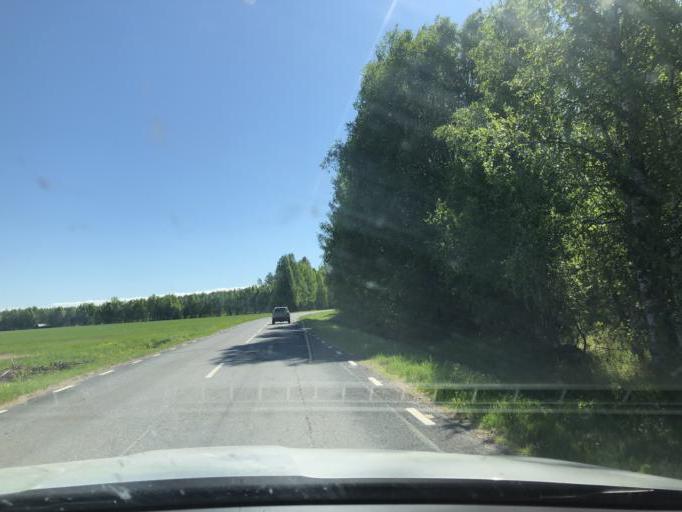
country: SE
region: Norrbotten
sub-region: Lulea Kommun
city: Gammelstad
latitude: 65.6597
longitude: 21.9898
